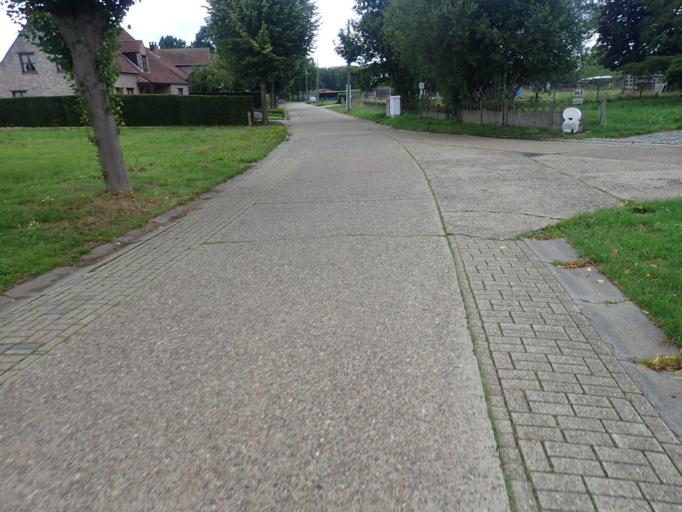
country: BE
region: Flanders
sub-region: Provincie Antwerpen
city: Lille
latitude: 51.2648
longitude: 4.7796
